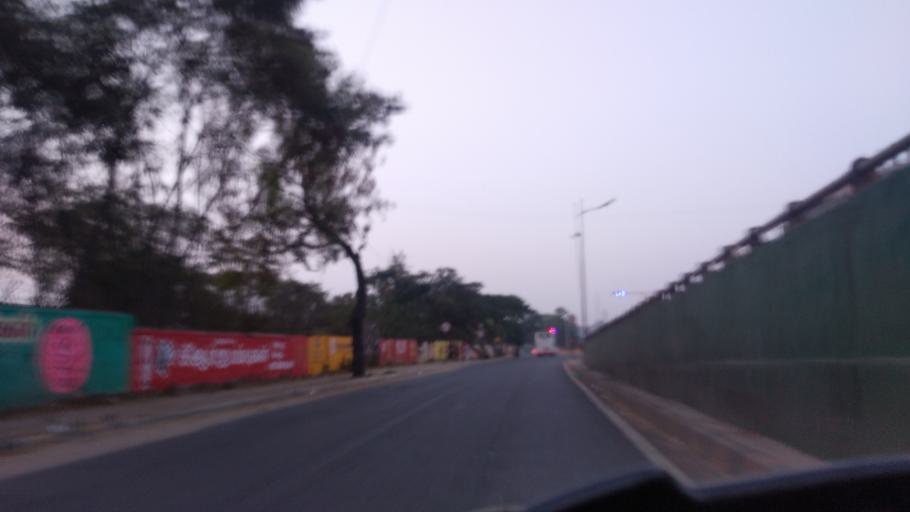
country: IN
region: Tamil Nadu
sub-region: Coimbatore
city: Coimbatore
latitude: 11.0101
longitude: 76.9675
